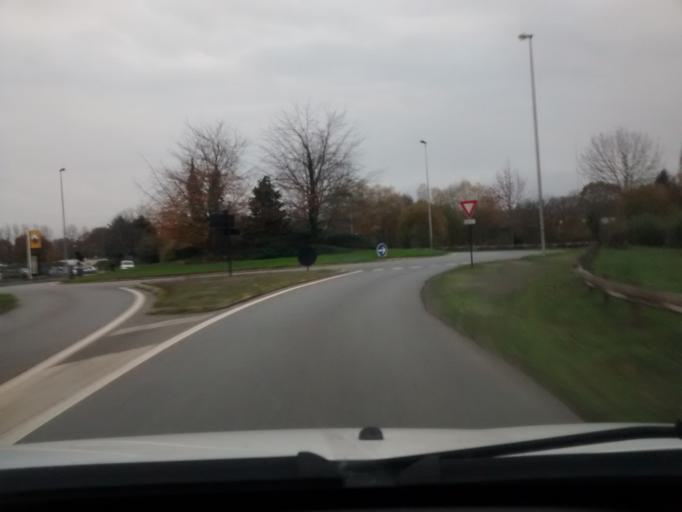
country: FR
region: Brittany
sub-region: Departement d'Ille-et-Vilaine
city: Acigne
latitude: 48.1358
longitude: -1.5445
